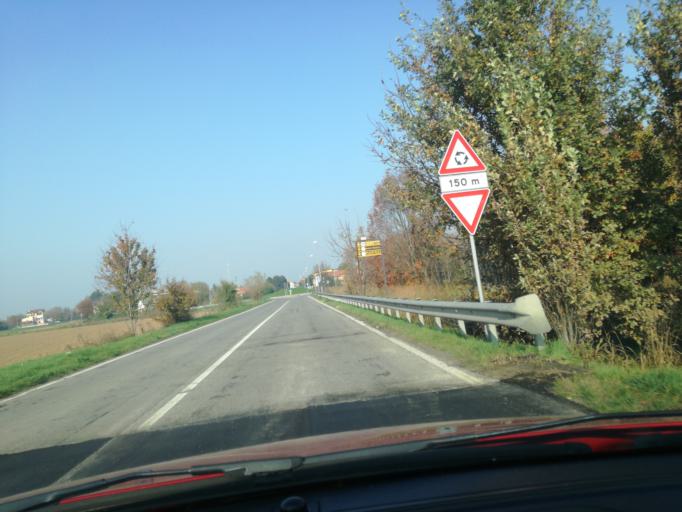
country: IT
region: Lombardy
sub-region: Provincia di Monza e Brianza
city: Ornago
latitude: 45.5921
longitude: 9.4157
